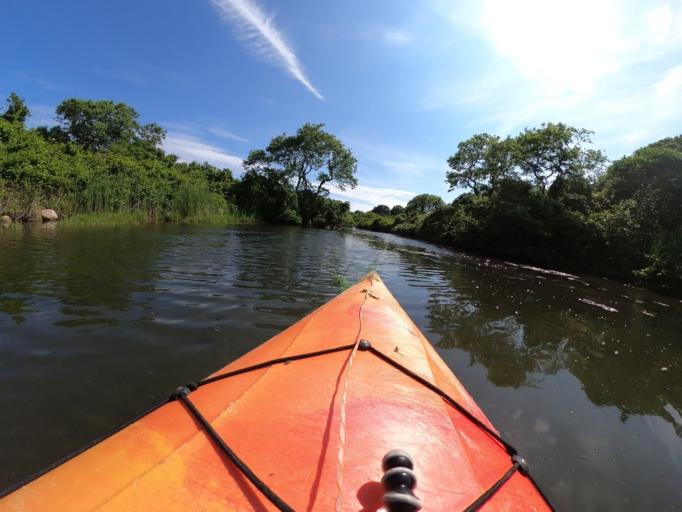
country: US
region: Massachusetts
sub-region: Dukes County
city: West Tisbury
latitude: 41.3288
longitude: -70.7862
